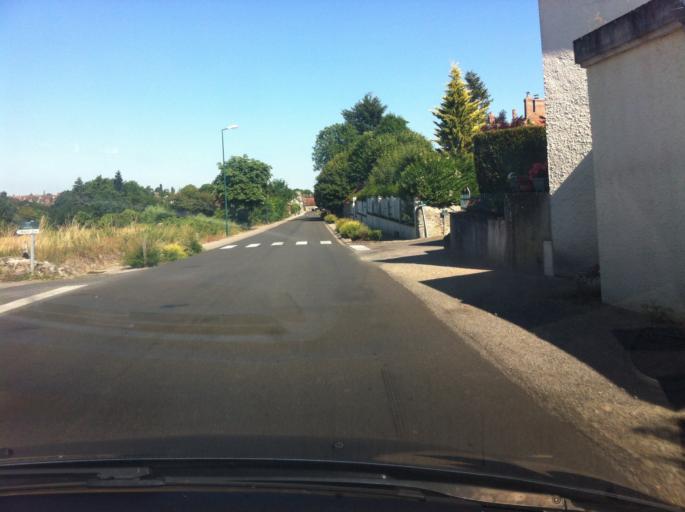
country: FR
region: Auvergne
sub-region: Departement de l'Allier
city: Chantelle
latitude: 46.2368
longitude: 3.1432
